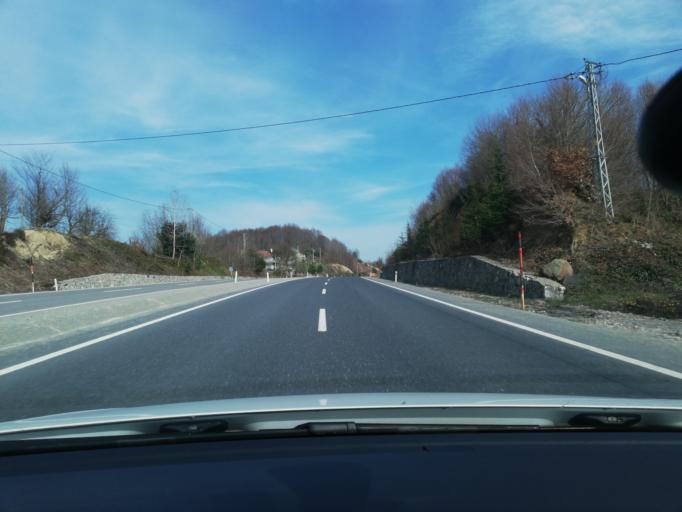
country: TR
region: Zonguldak
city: Kozlu
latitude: 41.3327
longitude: 31.6108
